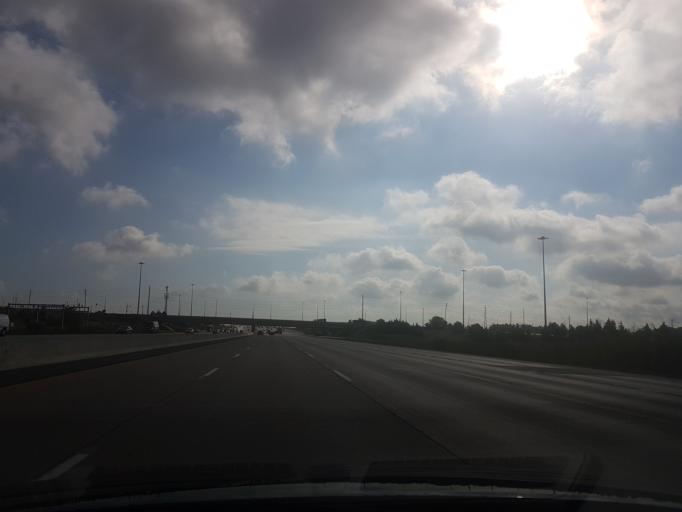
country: CA
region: Ontario
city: Concord
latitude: 43.7851
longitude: -79.5274
